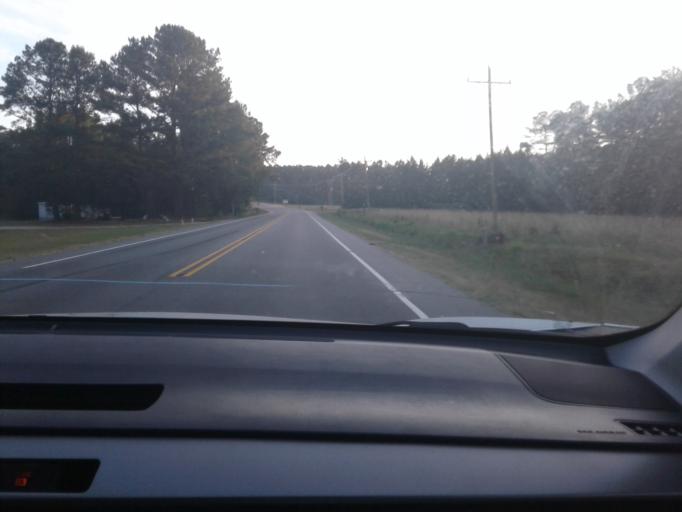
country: US
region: North Carolina
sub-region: Harnett County
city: Lillington
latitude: 35.4389
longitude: -78.8280
